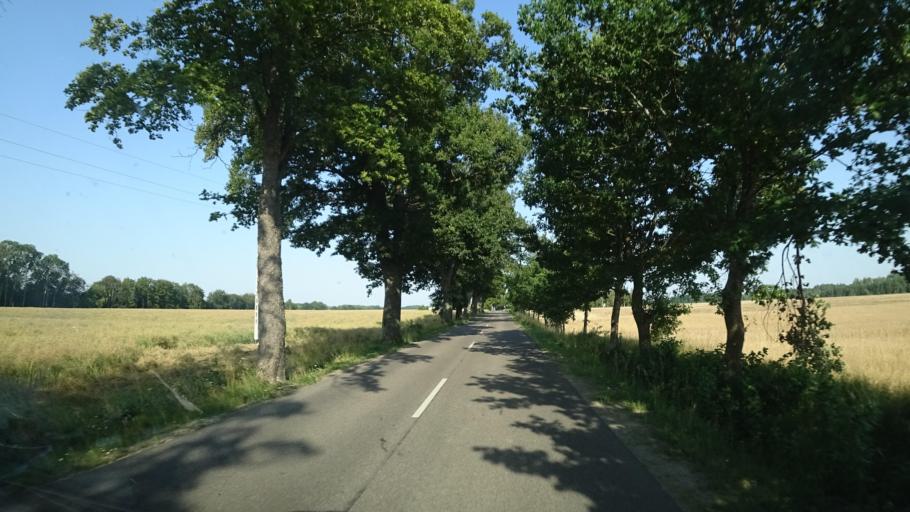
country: PL
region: Pomeranian Voivodeship
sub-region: Powiat czluchowski
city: Przechlewo
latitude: 53.8040
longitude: 17.3017
